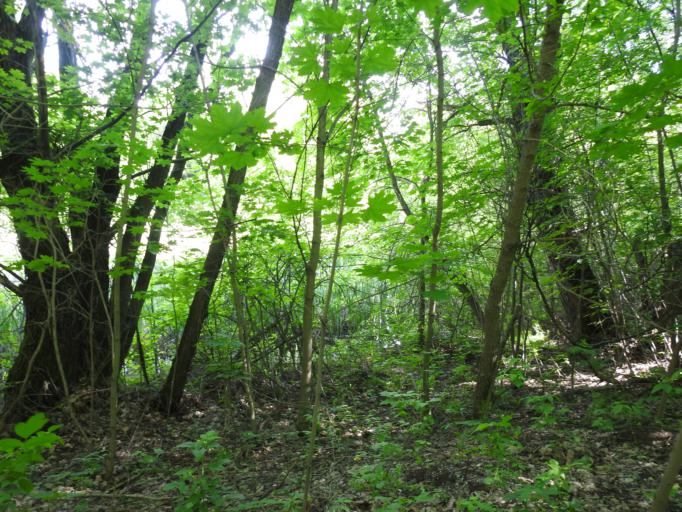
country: RU
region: Saratov
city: Engel's
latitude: 51.4702
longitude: 46.0765
